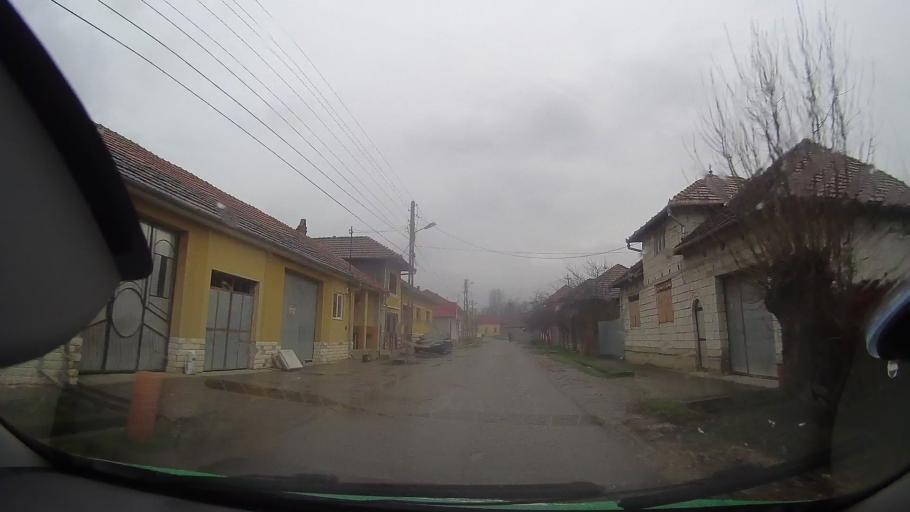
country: RO
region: Bihor
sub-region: Comuna Uileacu de Beius
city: Uileacu de Beius
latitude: 46.7089
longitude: 22.2255
